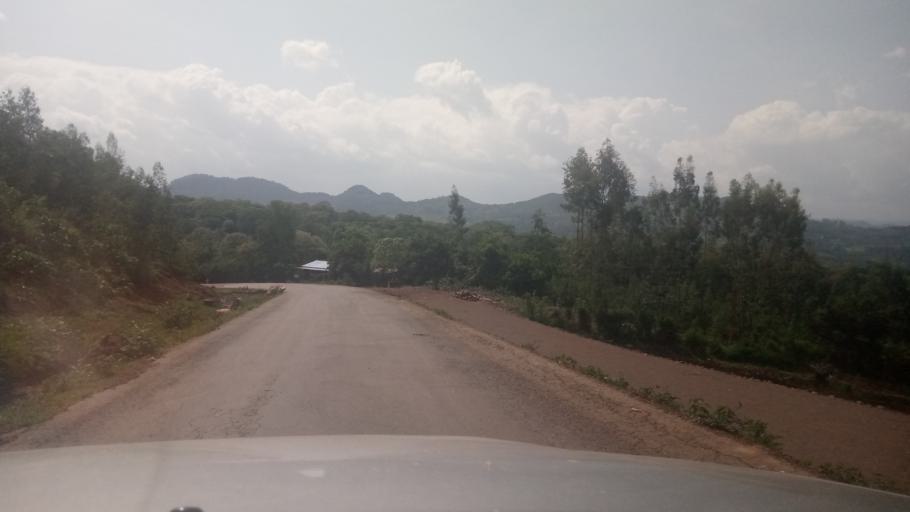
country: ET
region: Oromiya
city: Agaro
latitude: 7.9907
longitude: 36.5103
